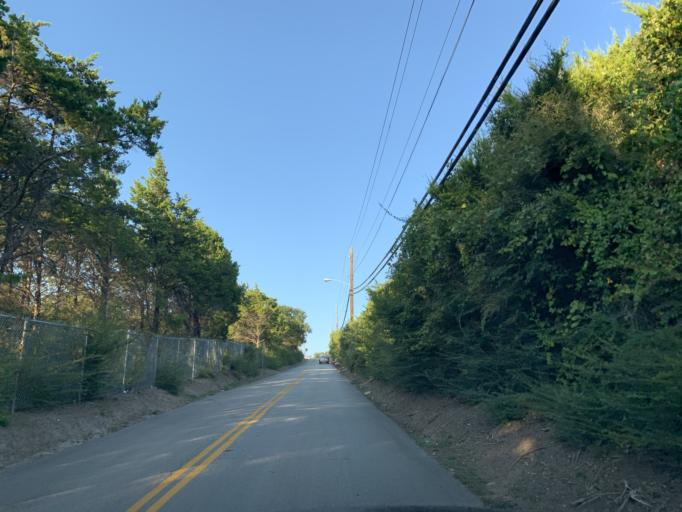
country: US
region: Texas
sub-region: Dallas County
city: Hutchins
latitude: 32.6715
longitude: -96.7859
